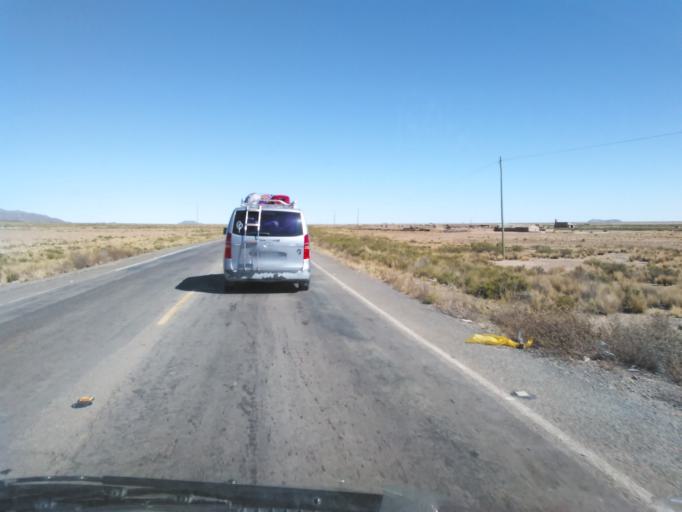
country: BO
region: Oruro
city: Machacamarca
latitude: -18.0778
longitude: -67.0064
